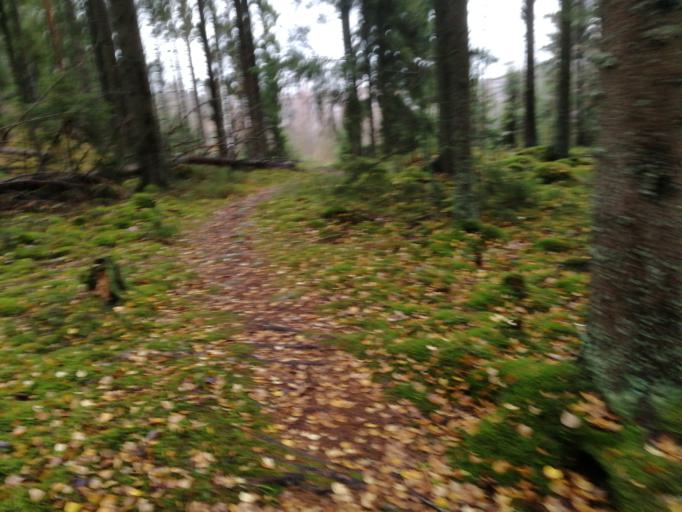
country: FI
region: Pirkanmaa
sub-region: Tampere
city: Tampere
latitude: 61.4564
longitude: 23.8813
